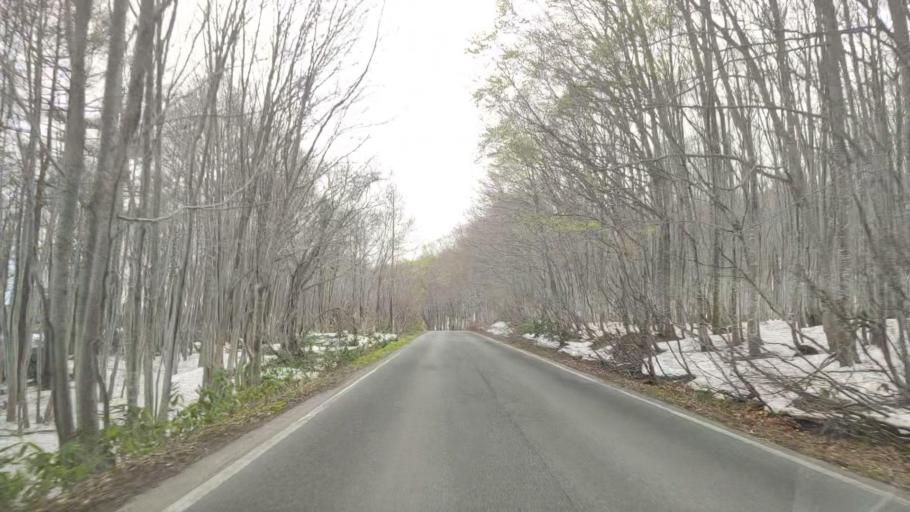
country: JP
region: Aomori
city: Aomori Shi
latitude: 40.6836
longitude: 140.9272
